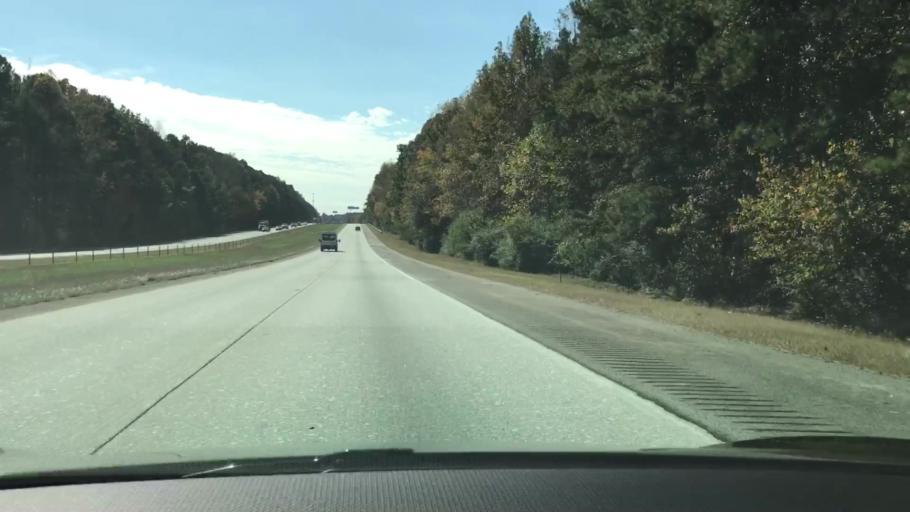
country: US
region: Georgia
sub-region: Gwinnett County
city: Buford
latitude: 34.1009
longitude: -83.9854
